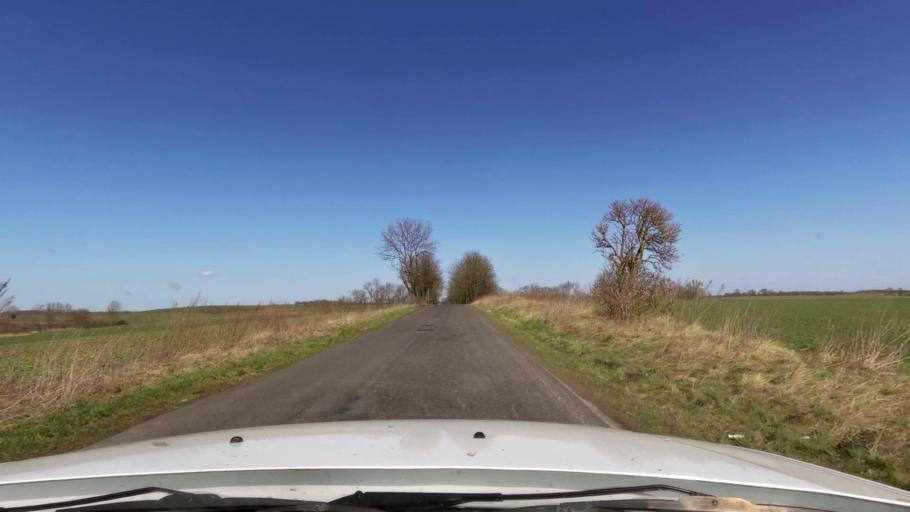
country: PL
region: West Pomeranian Voivodeship
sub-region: Powiat gryfinski
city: Cedynia
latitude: 52.8740
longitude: 14.2866
